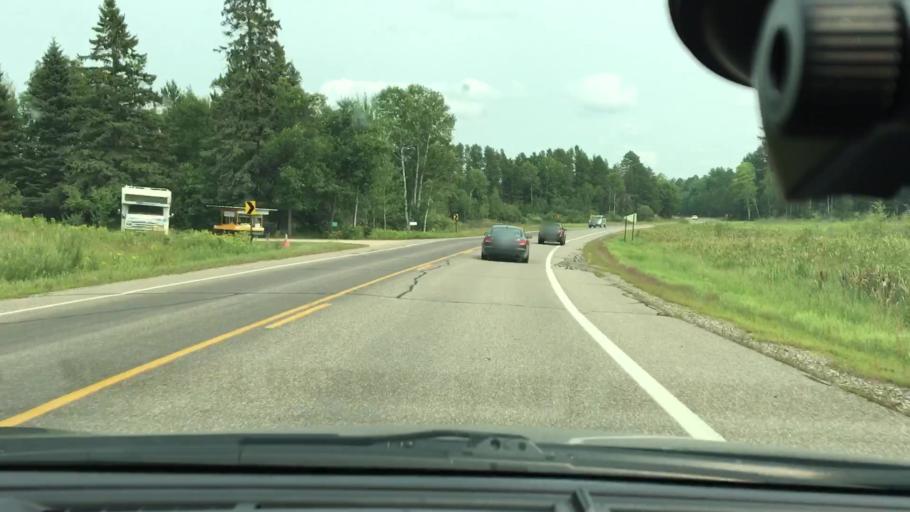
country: US
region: Minnesota
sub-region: Crow Wing County
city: Cross Lake
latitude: 46.7312
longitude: -94.0018
